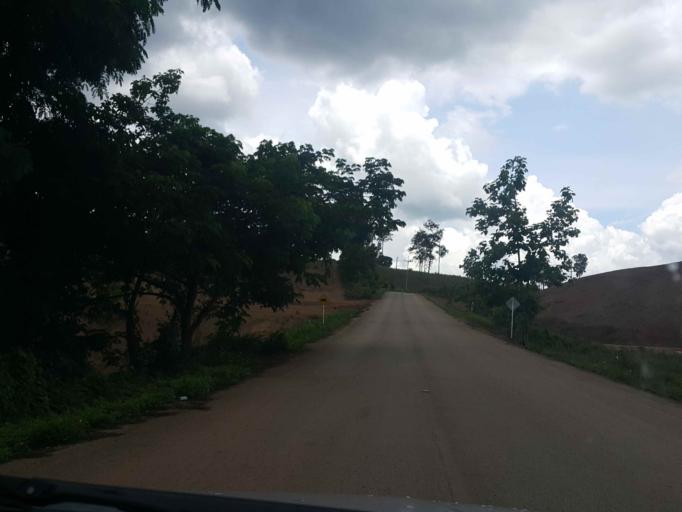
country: TH
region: Lampang
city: Ngao
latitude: 18.9495
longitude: 100.0773
